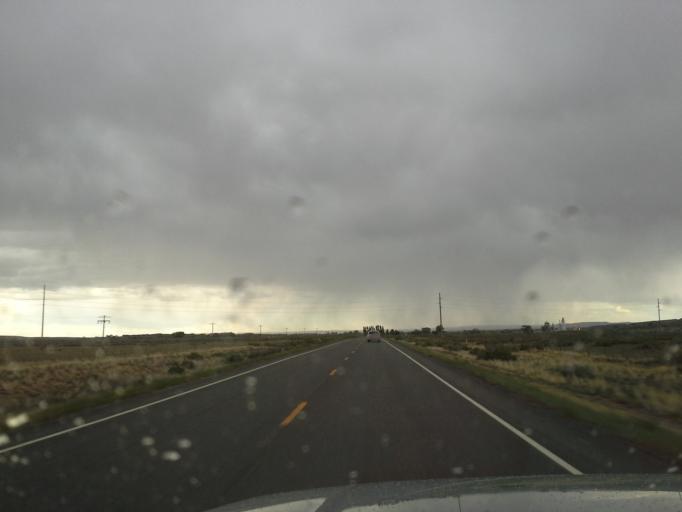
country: US
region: Wyoming
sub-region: Park County
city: Powell
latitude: 45.0143
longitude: -108.6272
